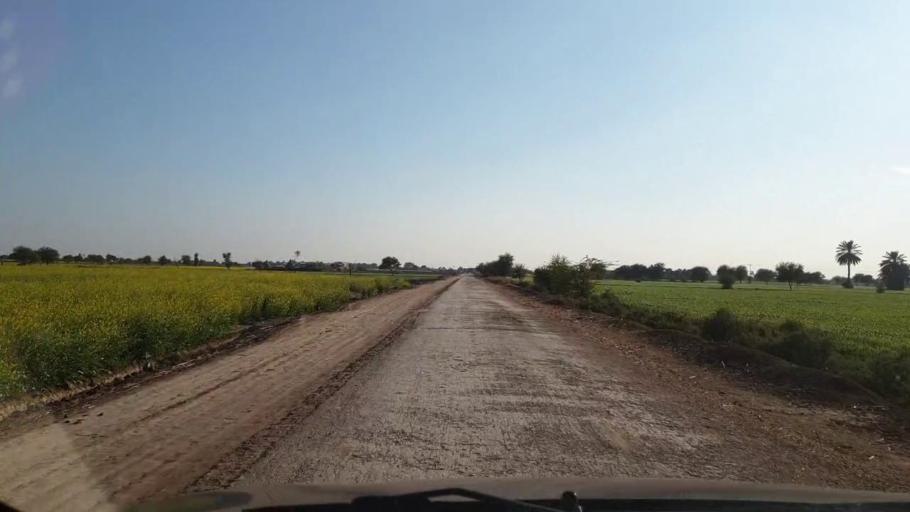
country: PK
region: Sindh
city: Jhol
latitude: 25.9607
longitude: 68.8615
